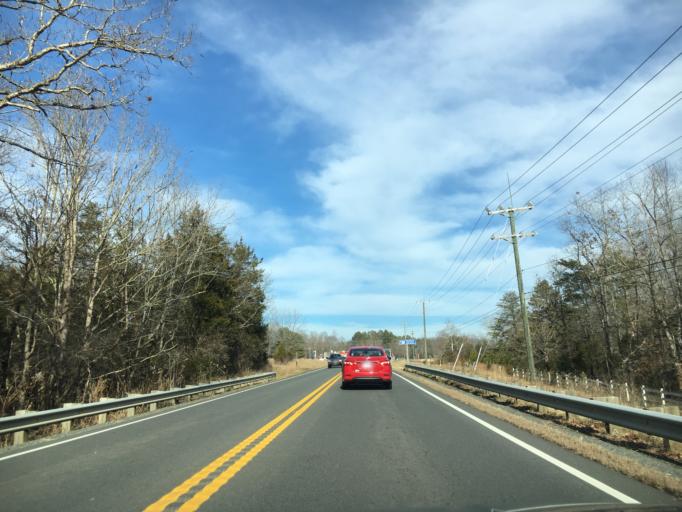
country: US
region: Virginia
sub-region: Fauquier County
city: Warrenton
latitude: 38.6749
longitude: -77.9187
